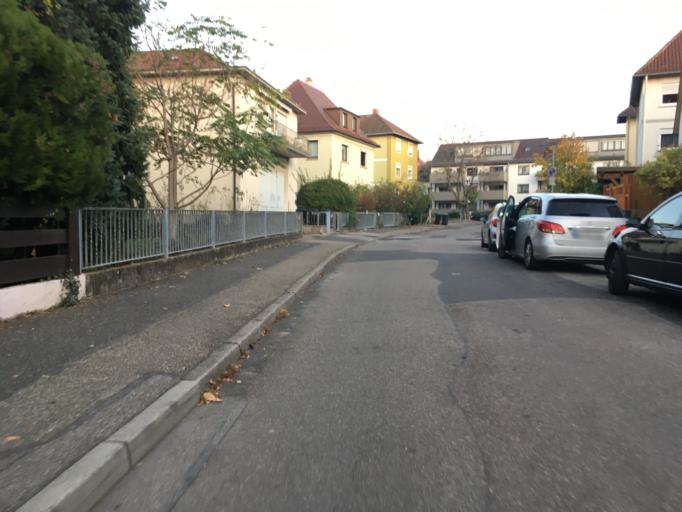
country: DE
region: Baden-Wuerttemberg
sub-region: Regierungsbezirk Stuttgart
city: Heilbronn
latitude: 49.1493
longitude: 9.2266
